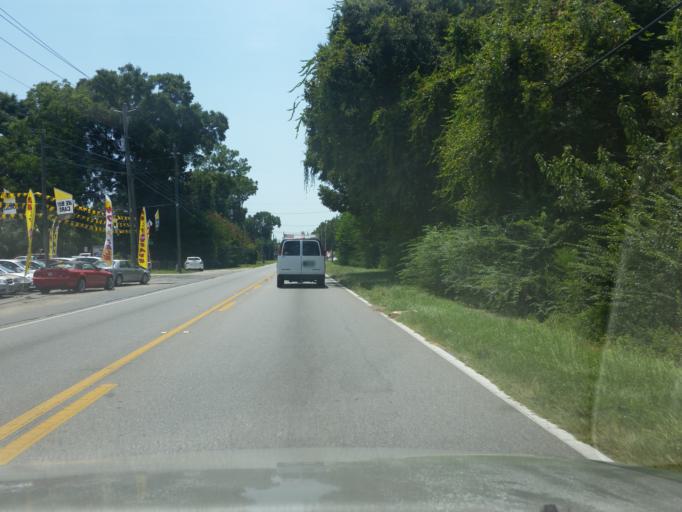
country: US
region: Florida
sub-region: Escambia County
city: Ensley
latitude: 30.4956
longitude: -87.2543
